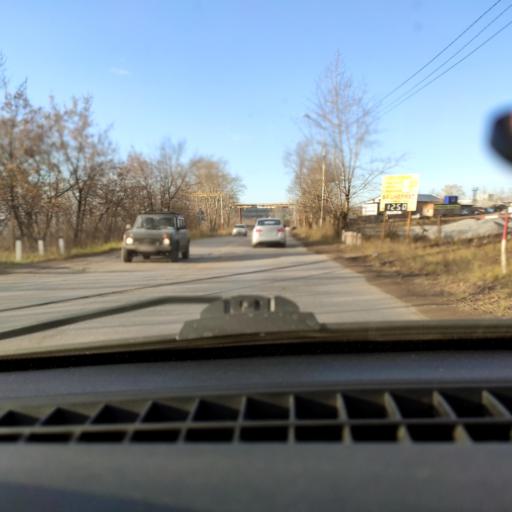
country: RU
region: Bashkortostan
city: Ufa
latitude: 54.8366
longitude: 56.0832
